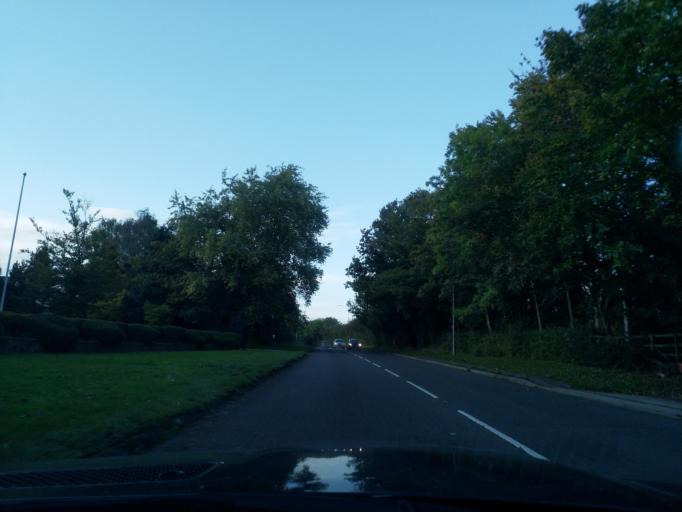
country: GB
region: England
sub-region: Warwickshire
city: Henley in Arden
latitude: 52.3376
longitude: -1.7729
